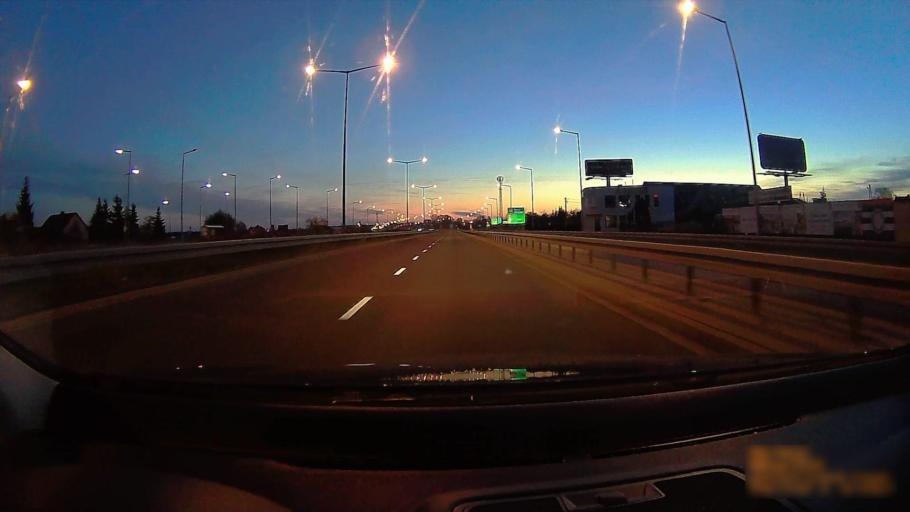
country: PL
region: Greater Poland Voivodeship
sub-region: Powiat koninski
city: Stare Miasto
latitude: 52.1846
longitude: 18.2273
